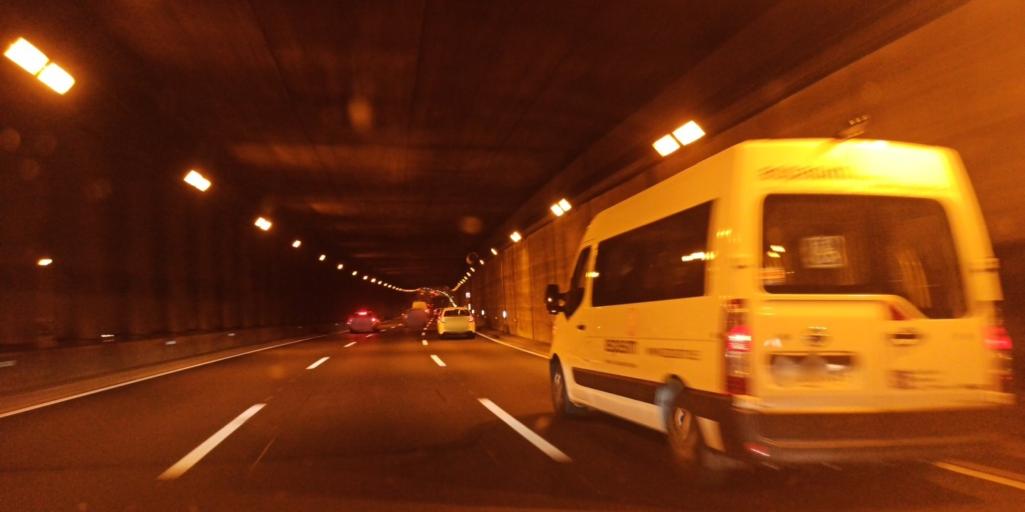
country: ES
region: Catalonia
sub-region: Provincia de Barcelona
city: les Corts
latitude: 41.3982
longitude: 2.1130
